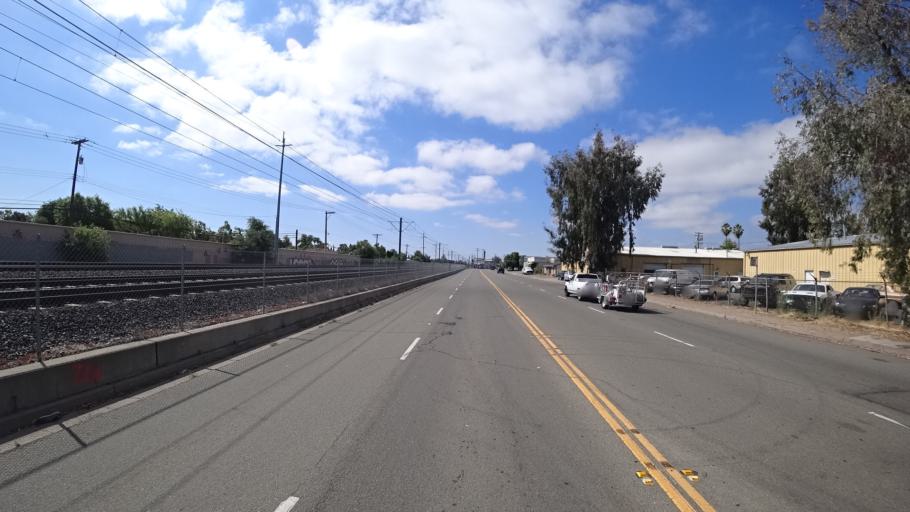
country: US
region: California
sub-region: Sacramento County
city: Sacramento
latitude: 38.5373
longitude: -121.4838
